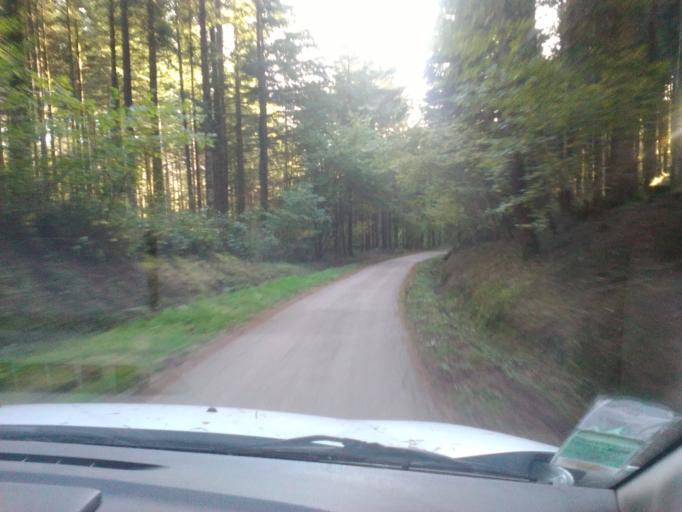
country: FR
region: Lorraine
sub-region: Departement des Vosges
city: Taintrux
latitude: 48.2560
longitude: 6.9172
